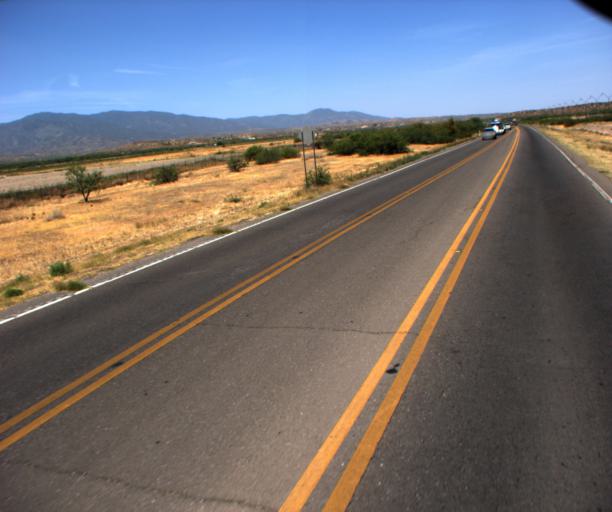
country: US
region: Arizona
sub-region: Gila County
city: Globe
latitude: 33.3559
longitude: -110.6696
